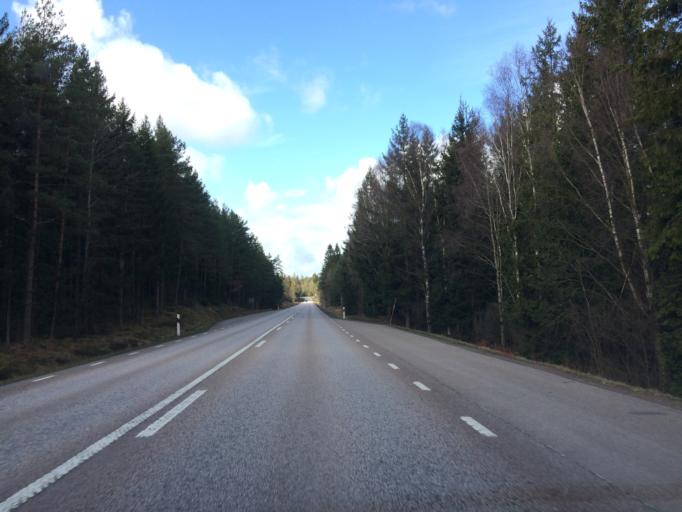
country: SE
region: Kronoberg
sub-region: Markaryds Kommun
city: Markaryd
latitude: 56.4868
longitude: 13.4767
